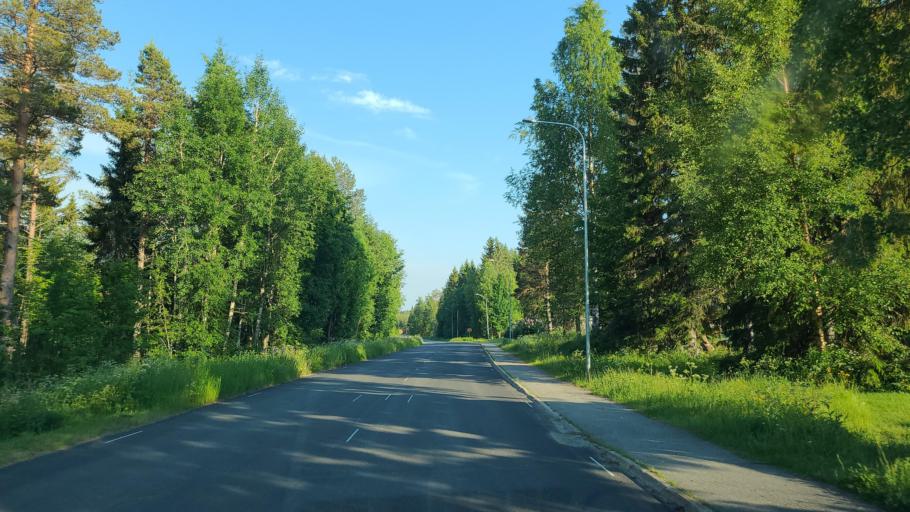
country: SE
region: Vaesterbotten
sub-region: Skelleftea Kommun
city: Burea
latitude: 64.3646
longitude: 21.3293
